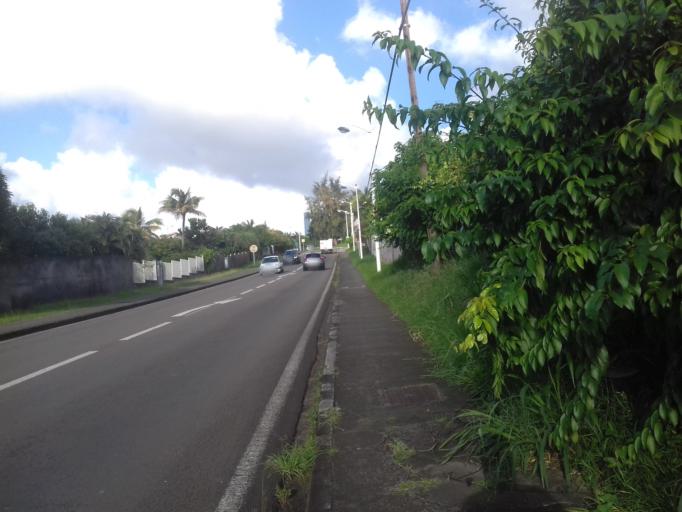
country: MQ
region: Martinique
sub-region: Martinique
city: Fort-de-France
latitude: 14.6177
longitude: -61.0967
